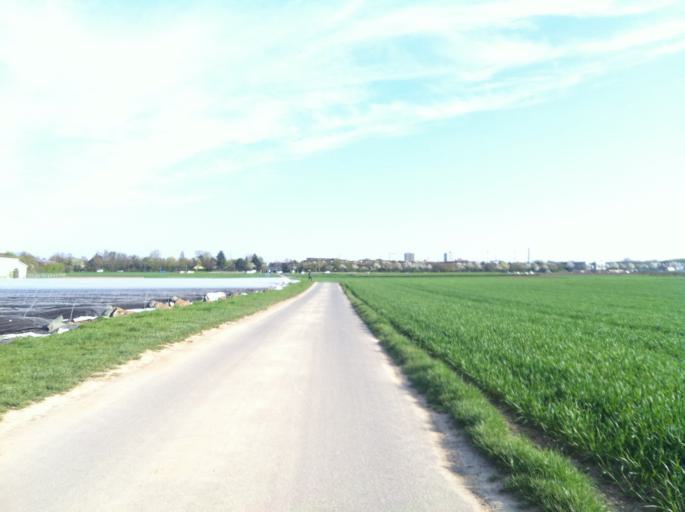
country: DE
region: Rheinland-Pfalz
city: Klein-Winternheim
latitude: 49.9768
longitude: 8.2285
